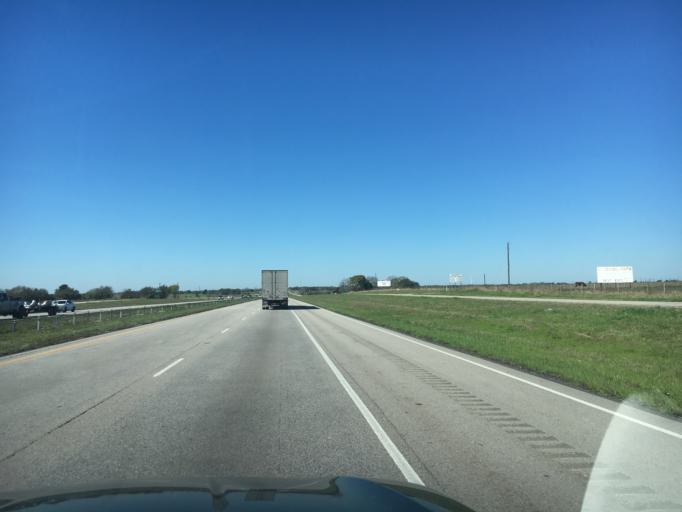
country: US
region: Texas
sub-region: Colorado County
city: Eagle Lake
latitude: 29.7325
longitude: -96.3756
